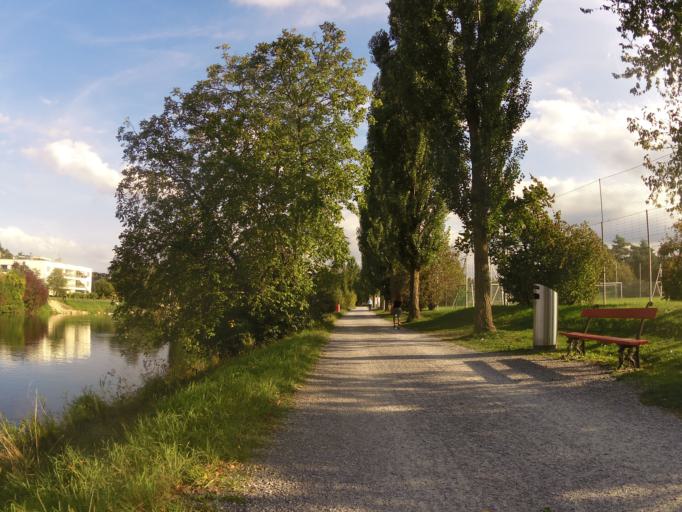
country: CH
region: Zurich
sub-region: Bezirk Zuerich
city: Zuerich (Kreis 10) / Hoengg
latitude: 47.3972
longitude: 8.5005
